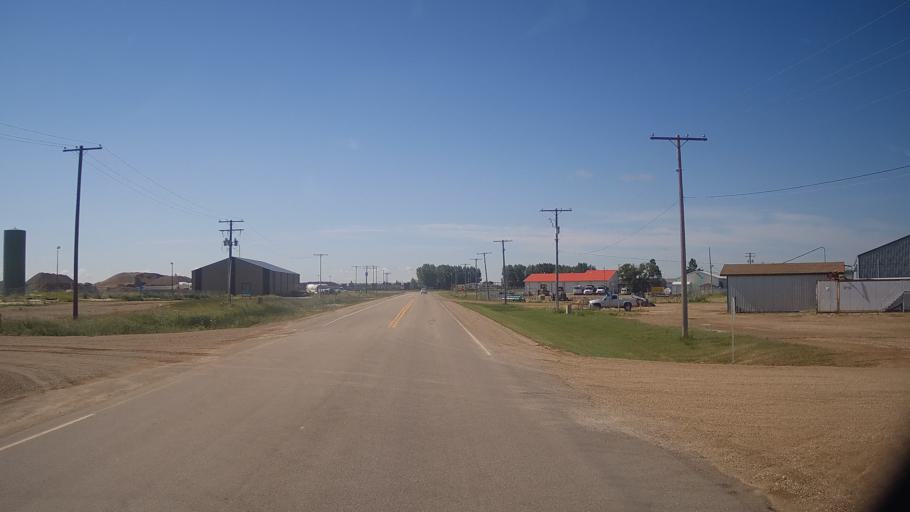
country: CA
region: Saskatchewan
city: Watrous
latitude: 51.6695
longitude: -105.4517
